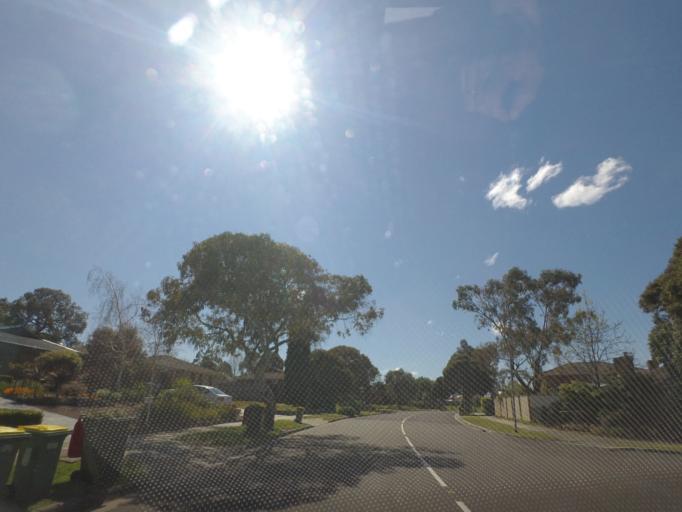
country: AU
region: Victoria
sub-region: Knox
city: Wantirna South
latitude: -37.8919
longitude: 145.2221
